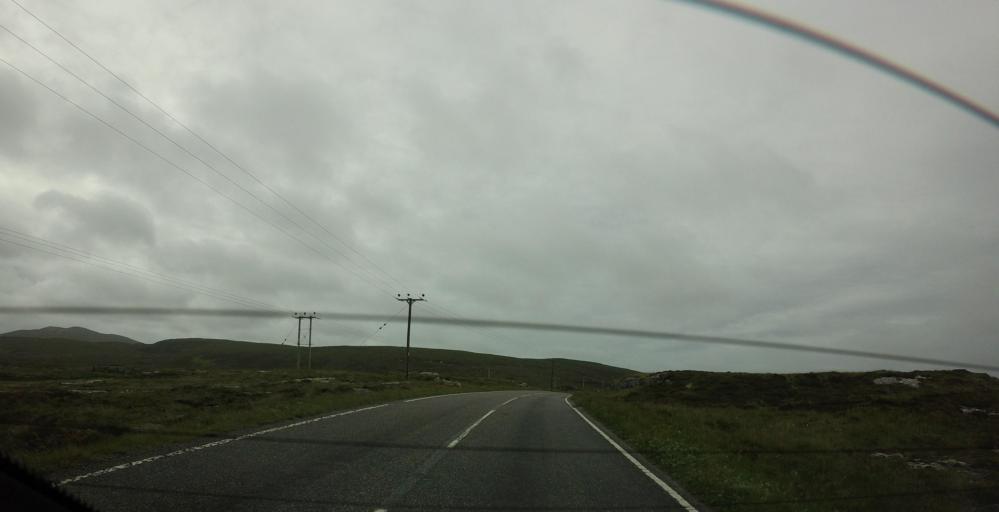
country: GB
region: Scotland
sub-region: Eilean Siar
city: Isle of South Uist
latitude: 57.2406
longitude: -7.3856
